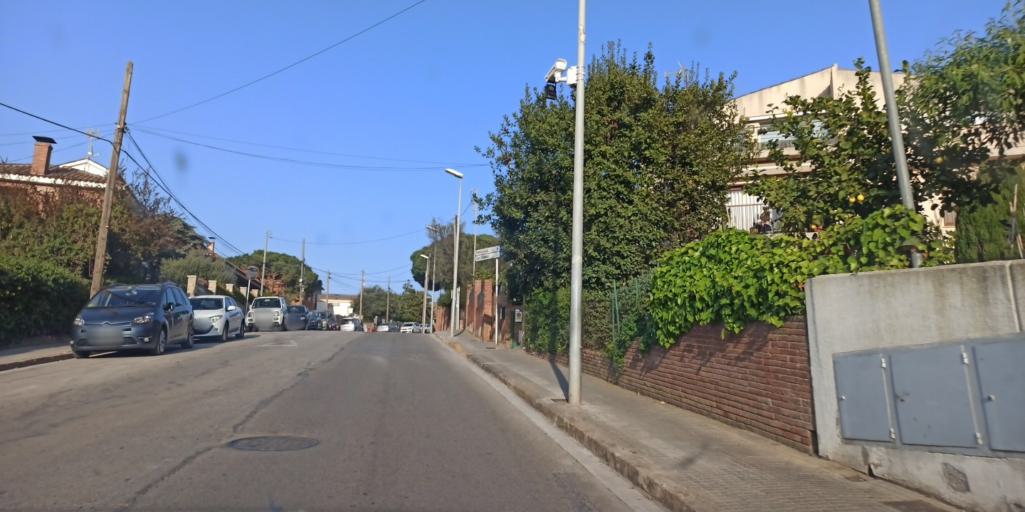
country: ES
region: Catalonia
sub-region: Provincia de Barcelona
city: Sant Just Desvern
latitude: 41.3876
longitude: 2.0746
